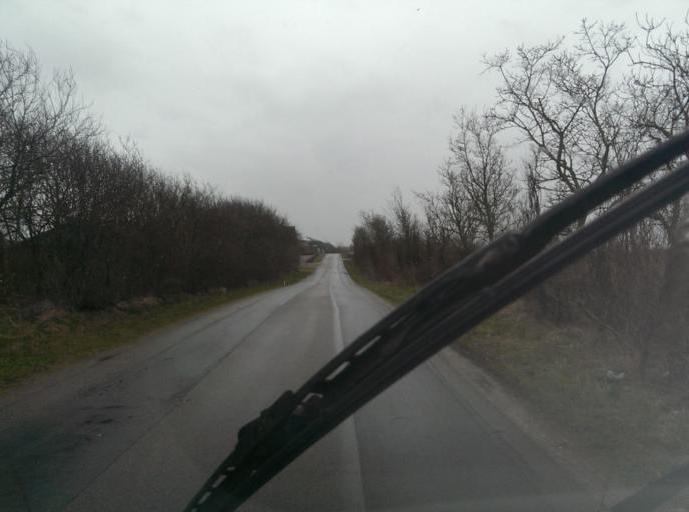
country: DK
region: Central Jutland
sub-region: Ringkobing-Skjern Kommune
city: Skjern
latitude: 56.0103
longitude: 8.4176
